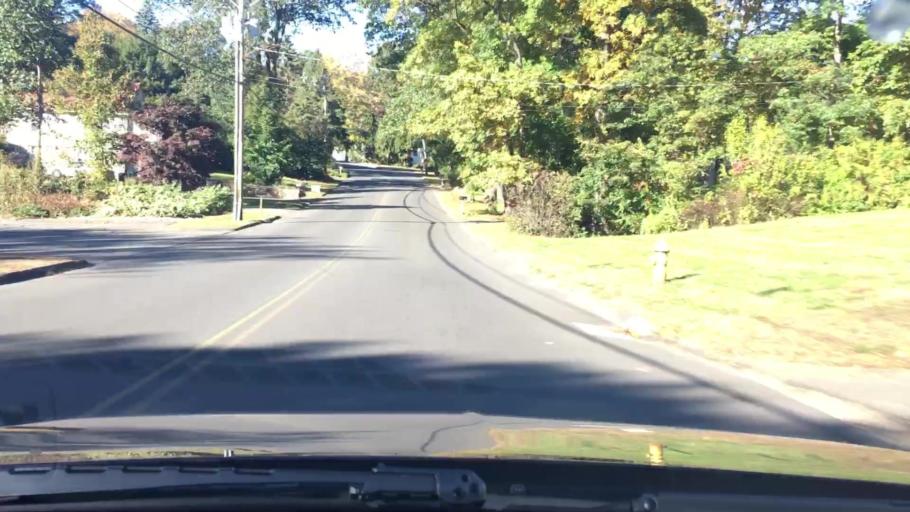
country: US
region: Connecticut
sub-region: New Haven County
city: Prospect
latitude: 41.5470
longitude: -72.9584
